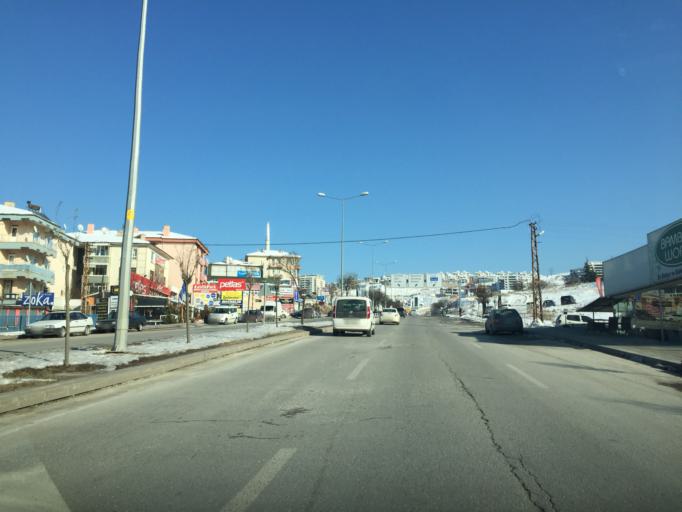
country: TR
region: Ankara
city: Batikent
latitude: 39.8850
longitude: 32.6958
